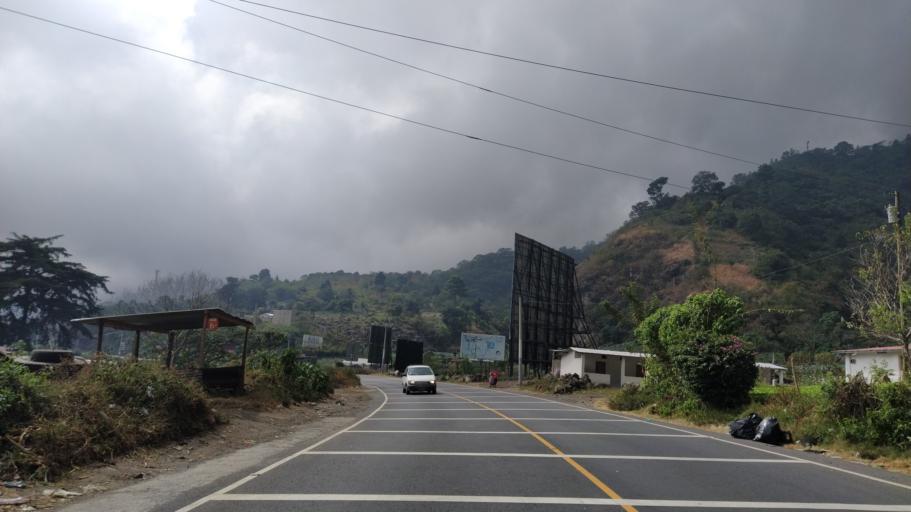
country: GT
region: Quetzaltenango
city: Zunil
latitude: 14.7531
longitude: -91.5085
